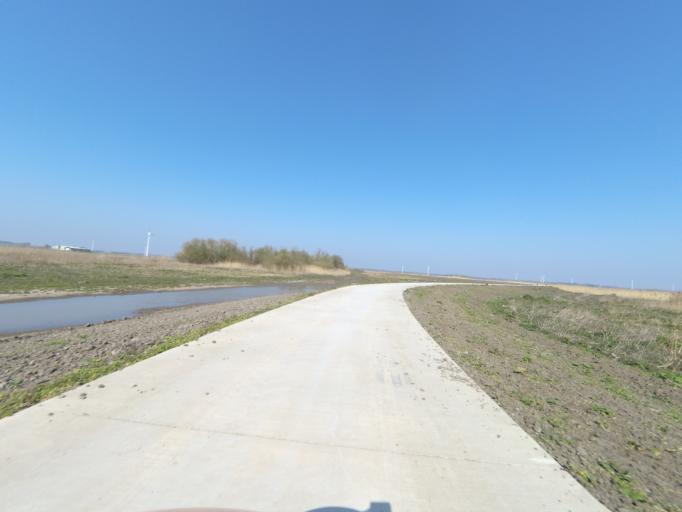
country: NL
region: Utrecht
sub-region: Gemeente Bunschoten
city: Spakenburg
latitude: 52.3747
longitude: 5.3716
